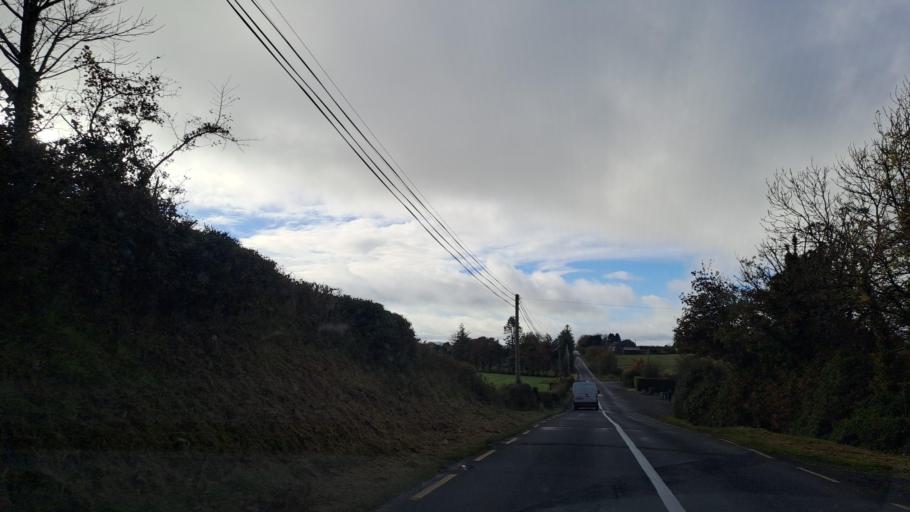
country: IE
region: Ulster
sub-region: An Cabhan
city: Virginia
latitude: 53.8466
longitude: -7.0652
